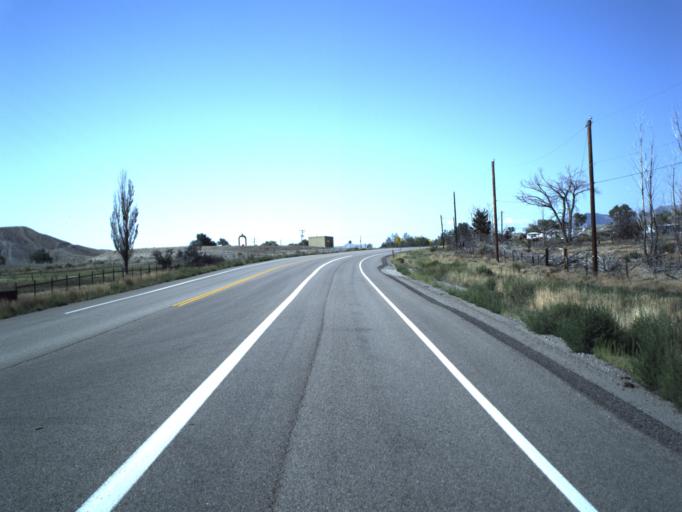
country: US
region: Utah
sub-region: Emery County
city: Ferron
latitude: 39.1323
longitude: -111.1004
